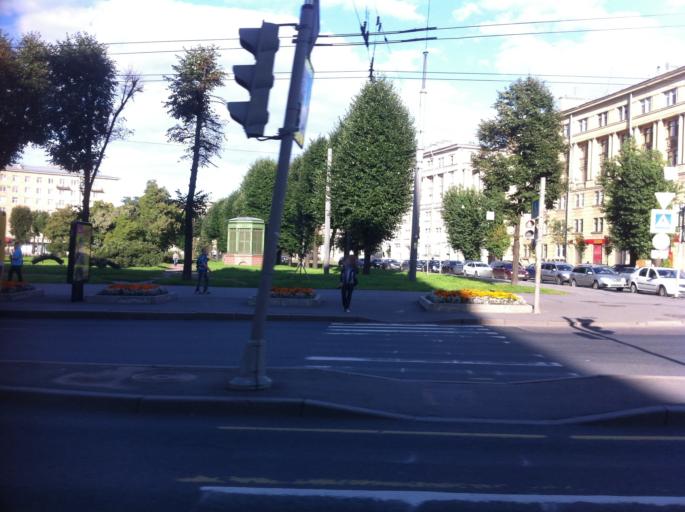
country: RU
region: St.-Petersburg
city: Avtovo
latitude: 59.8732
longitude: 30.2587
